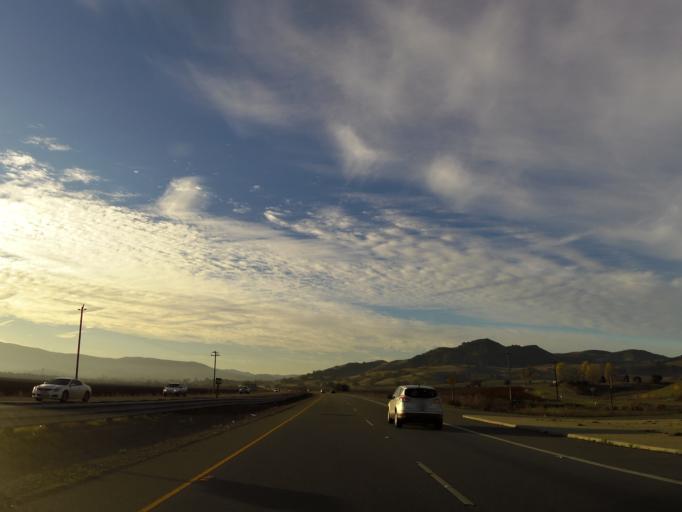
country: US
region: California
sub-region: Santa Clara County
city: Gilroy
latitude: 36.9507
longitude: -121.5527
